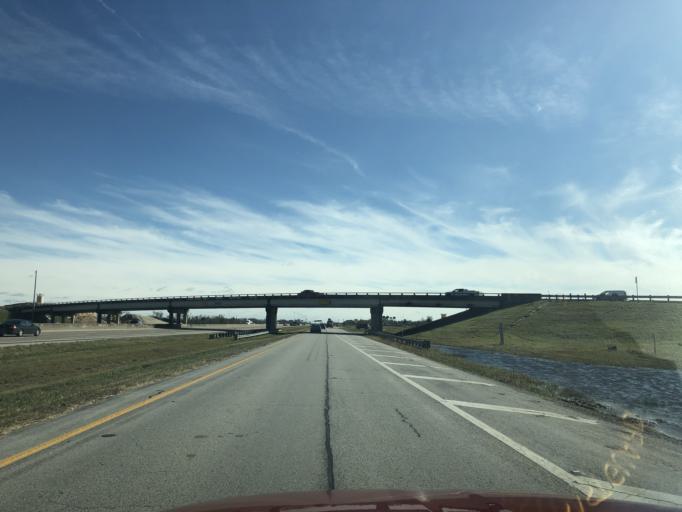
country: US
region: Texas
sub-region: Galveston County
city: Dickinson
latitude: 29.4312
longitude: -95.0617
